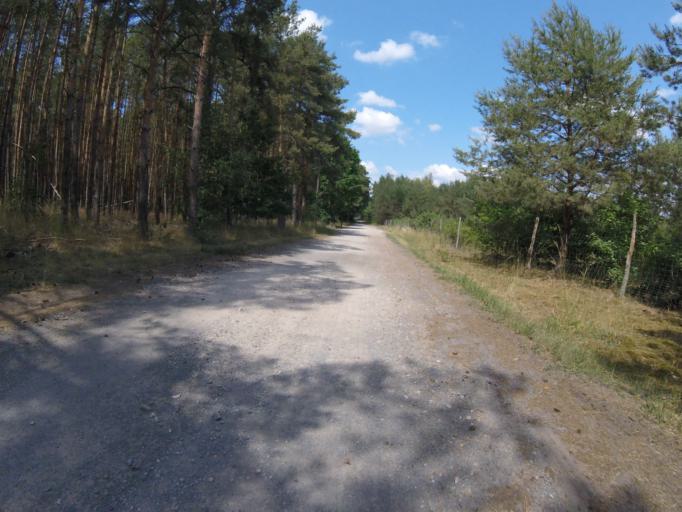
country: DE
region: Brandenburg
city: Bestensee
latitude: 52.2434
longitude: 13.6932
